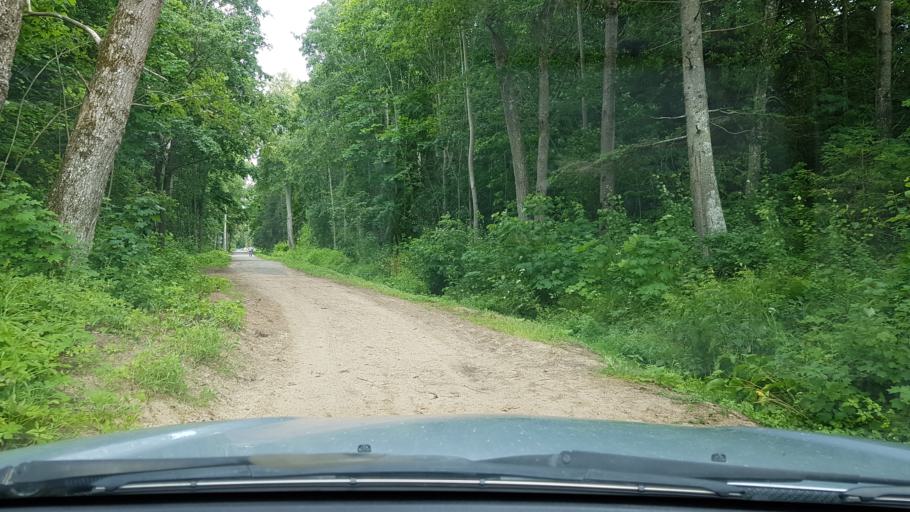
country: EE
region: Ida-Virumaa
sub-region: Narva-Joesuu linn
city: Narva-Joesuu
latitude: 59.4518
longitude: 28.0227
